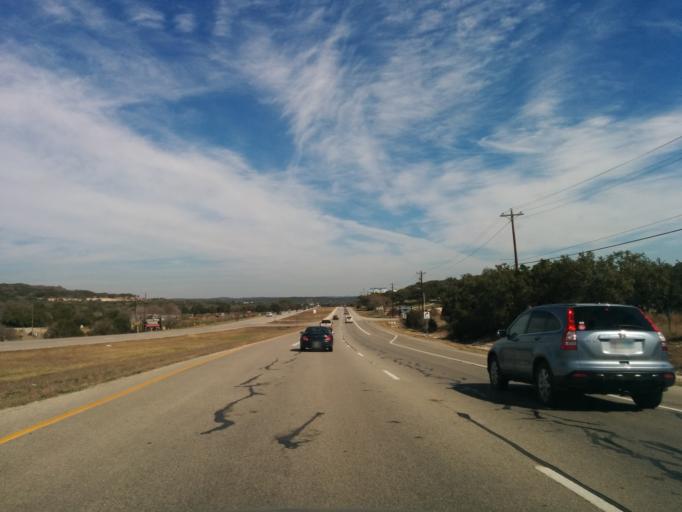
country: US
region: Texas
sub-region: Comal County
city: Bulverde
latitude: 29.8274
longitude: -98.4156
